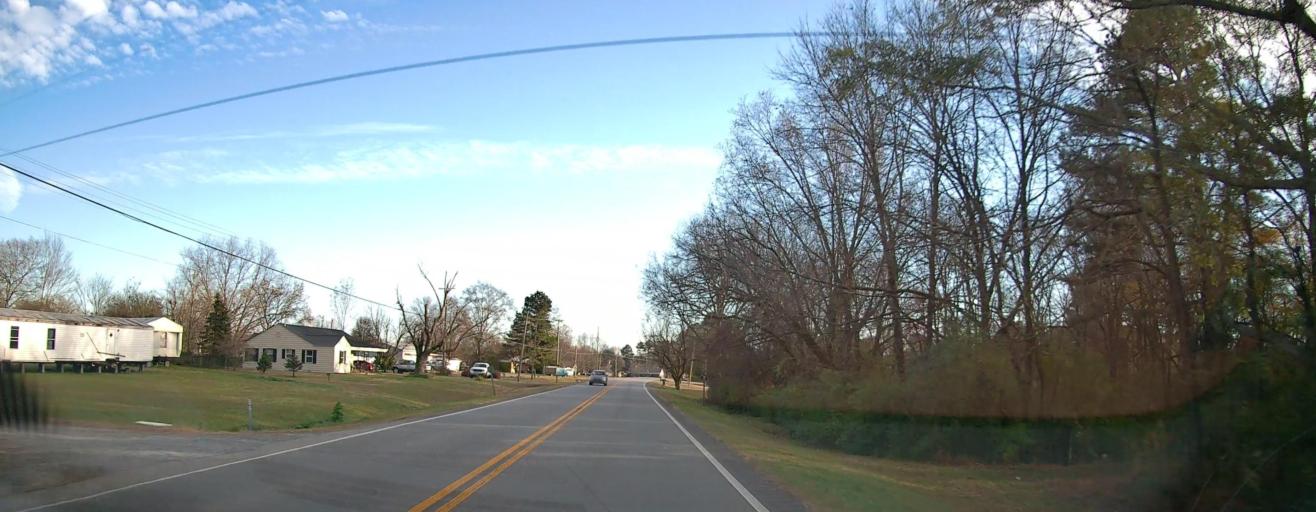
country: US
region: Alabama
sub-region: Marshall County
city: Arab
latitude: 34.3109
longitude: -86.5983
